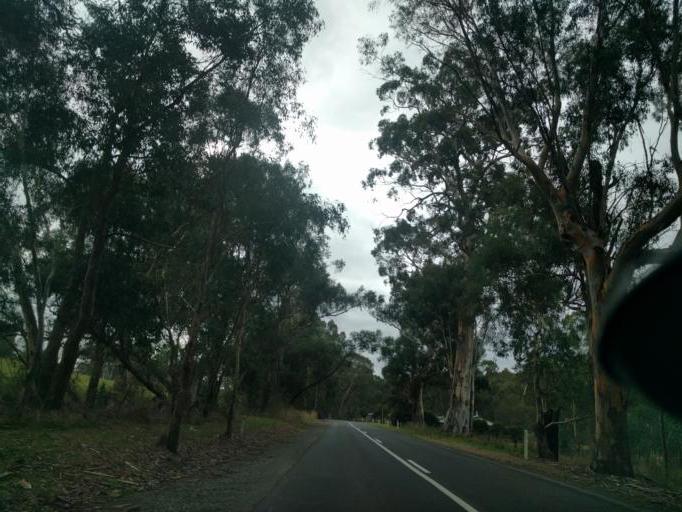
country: AU
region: South Australia
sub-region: Mount Barker
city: Hahndorf
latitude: -35.0672
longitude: 138.7731
